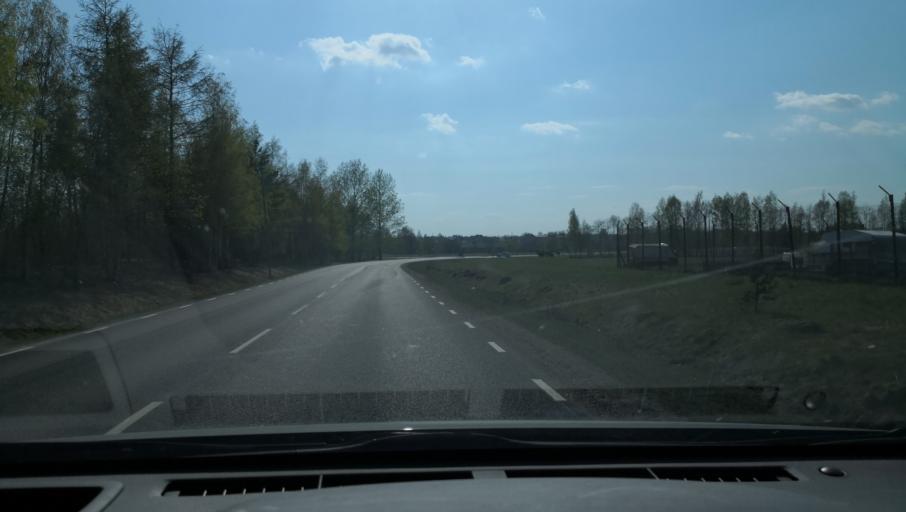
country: SE
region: Vaestmanland
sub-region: Sala Kommun
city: Sala
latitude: 59.9309
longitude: 16.6084
